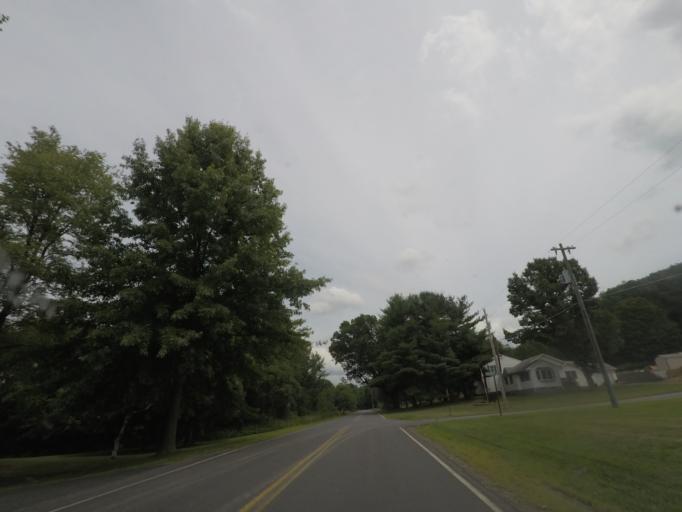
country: US
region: New York
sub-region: Rensselaer County
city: Wynantskill
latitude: 42.6994
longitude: -73.6209
